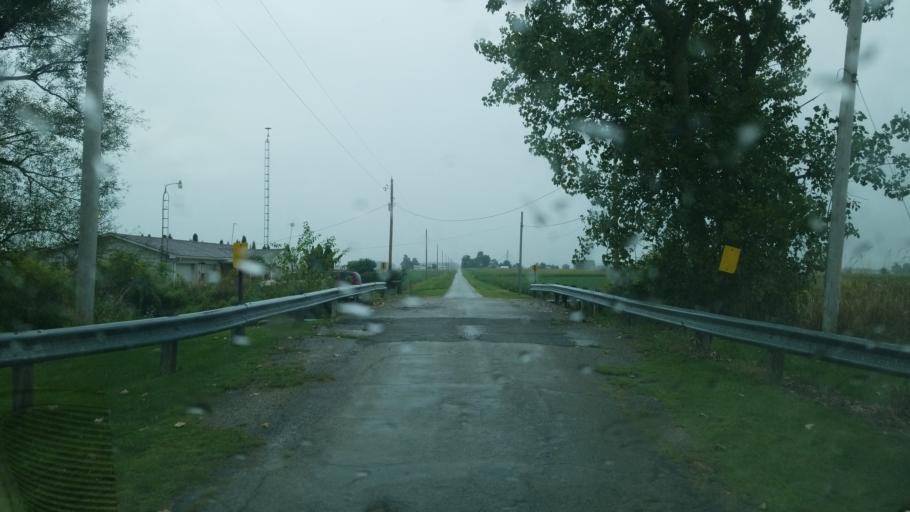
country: US
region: Ohio
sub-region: Huron County
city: Willard
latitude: 41.0102
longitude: -82.7876
